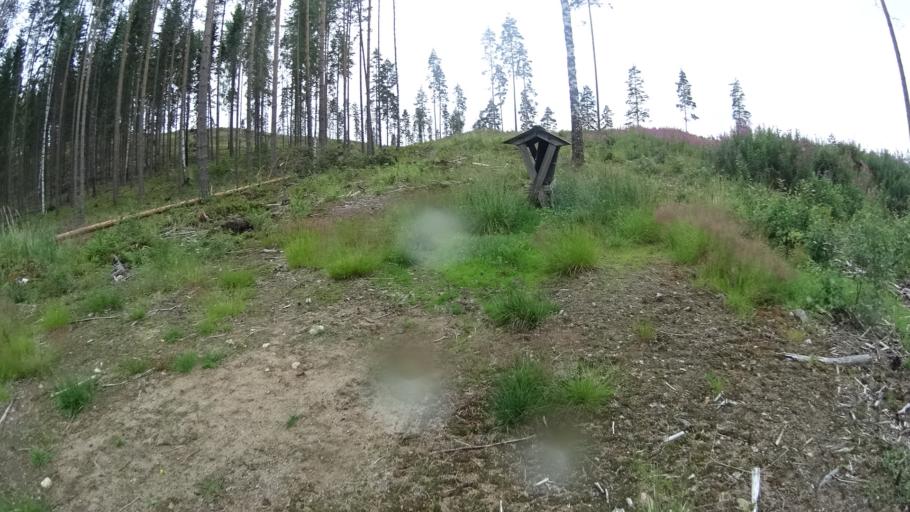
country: FI
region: Uusimaa
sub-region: Helsinki
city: Karkkila
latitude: 60.5956
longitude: 24.1819
